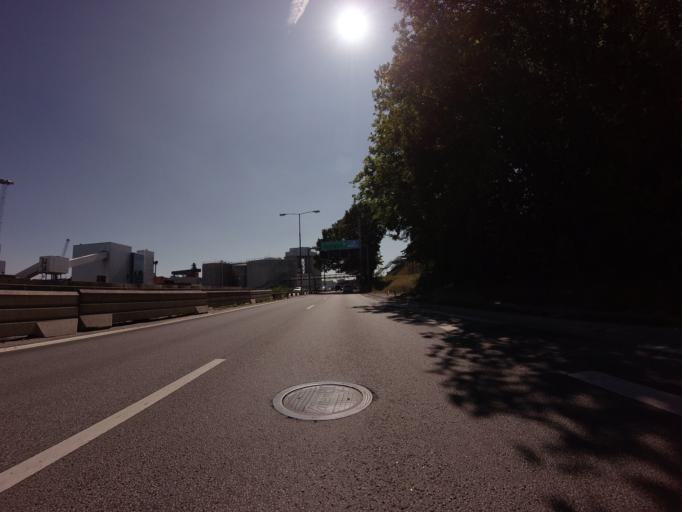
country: SE
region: Stockholm
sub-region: Stockholms Kommun
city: OEstermalm
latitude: 59.3547
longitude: 18.1055
